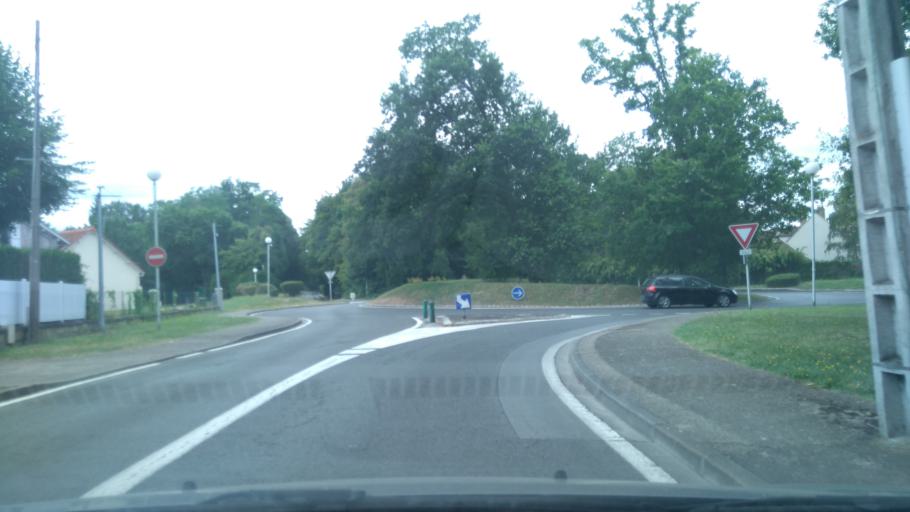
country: FR
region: Picardie
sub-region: Departement de l'Oise
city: Gouvieux
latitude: 49.1838
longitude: 2.4065
